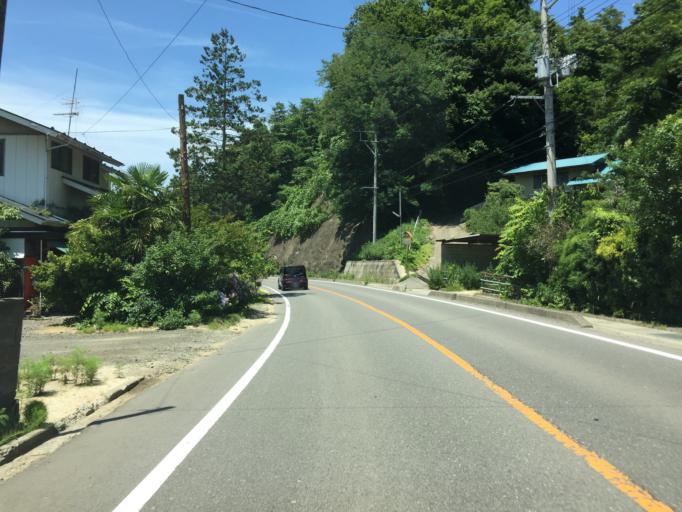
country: JP
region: Fukushima
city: Hobaramachi
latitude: 37.7631
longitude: 140.6215
